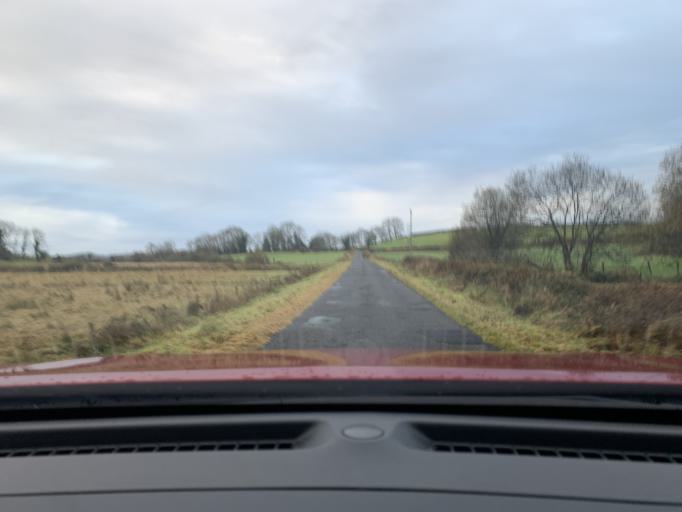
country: IE
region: Connaught
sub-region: Sligo
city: Ballymote
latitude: 54.0095
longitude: -8.4891
